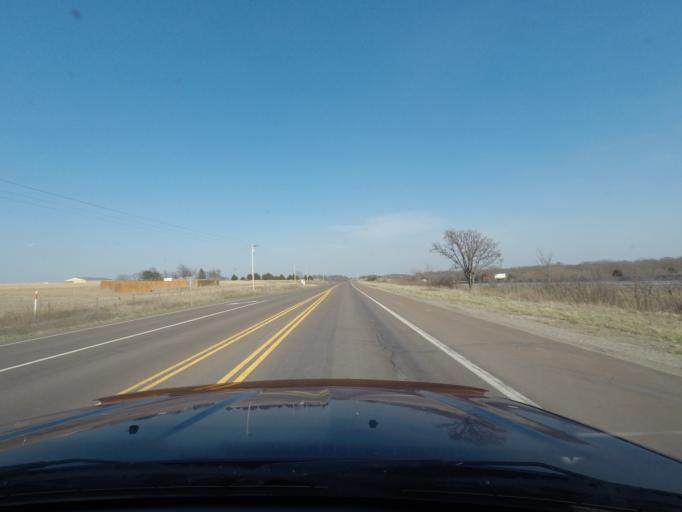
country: US
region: Kansas
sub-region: Douglas County
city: Lawrence
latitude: 39.0006
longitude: -95.3763
